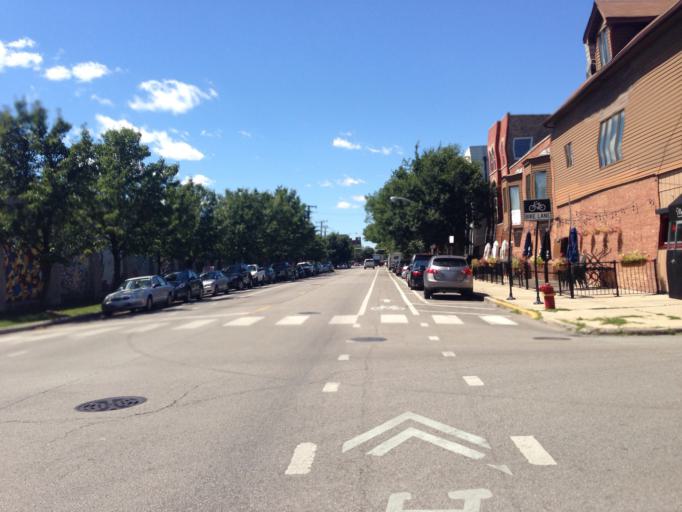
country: US
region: Illinois
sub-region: Cook County
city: Chicago
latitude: 41.8900
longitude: -87.6573
